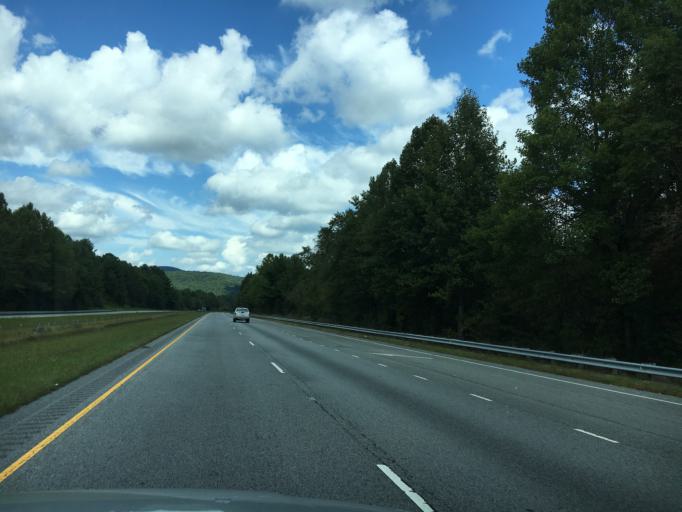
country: US
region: North Carolina
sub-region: Henderson County
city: Flat Rock
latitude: 35.1930
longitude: -82.4499
